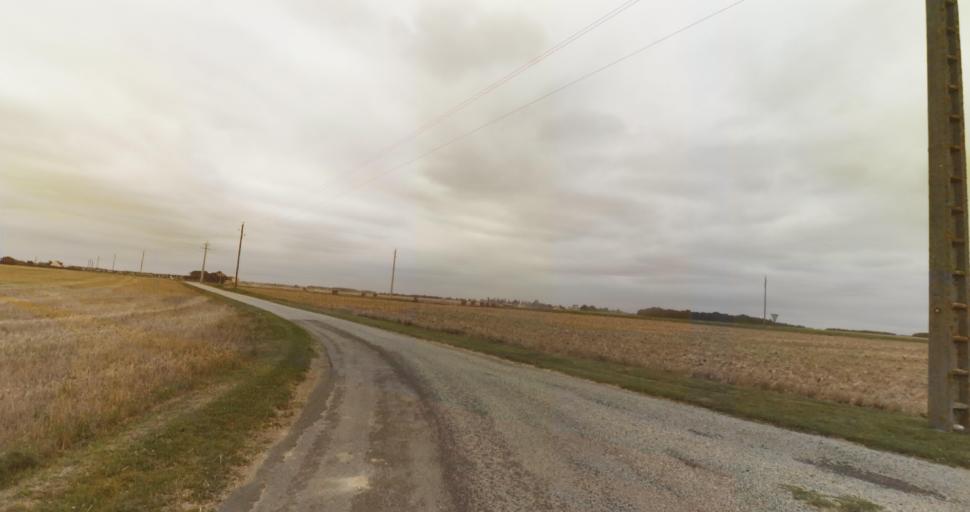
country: FR
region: Haute-Normandie
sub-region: Departement de l'Eure
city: Marcilly-sur-Eure
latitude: 48.9178
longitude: 1.3055
